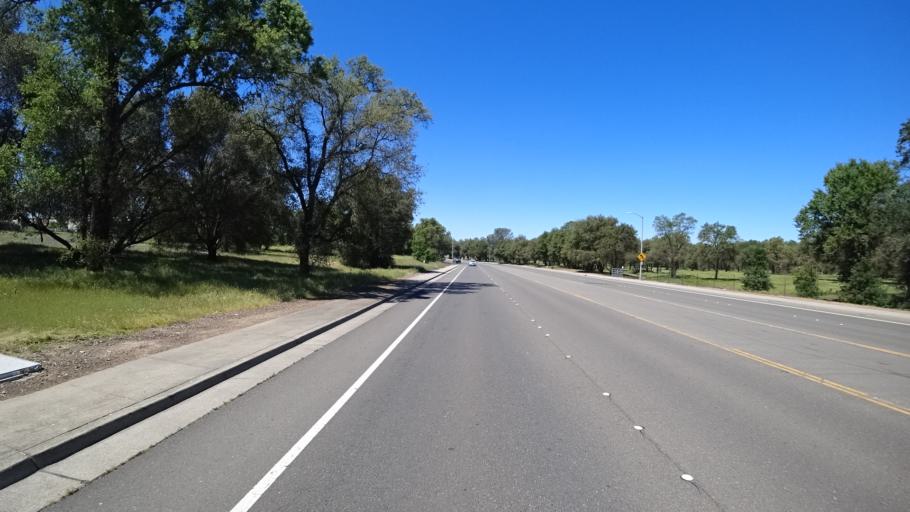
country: US
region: California
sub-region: Placer County
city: Loomis
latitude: 38.8065
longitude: -121.2074
